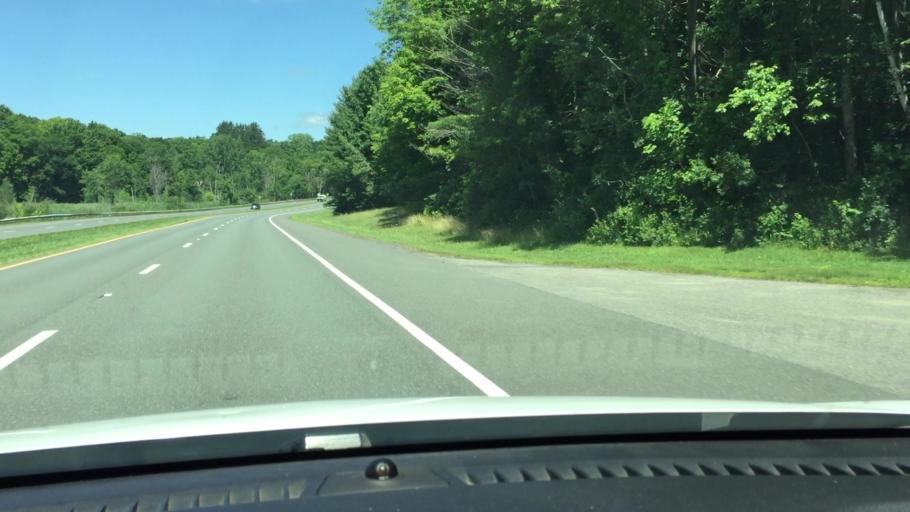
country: US
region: Massachusetts
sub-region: Berkshire County
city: Lenox
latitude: 42.3591
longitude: -73.2721
